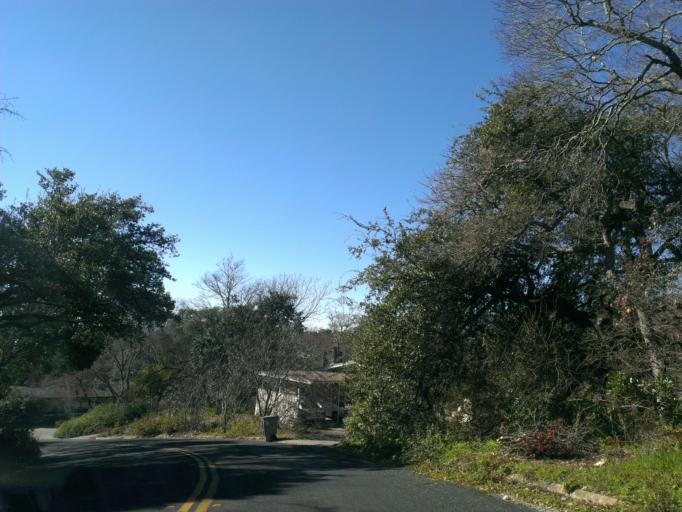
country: US
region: Texas
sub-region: Travis County
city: West Lake Hills
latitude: 30.3311
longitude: -97.7661
